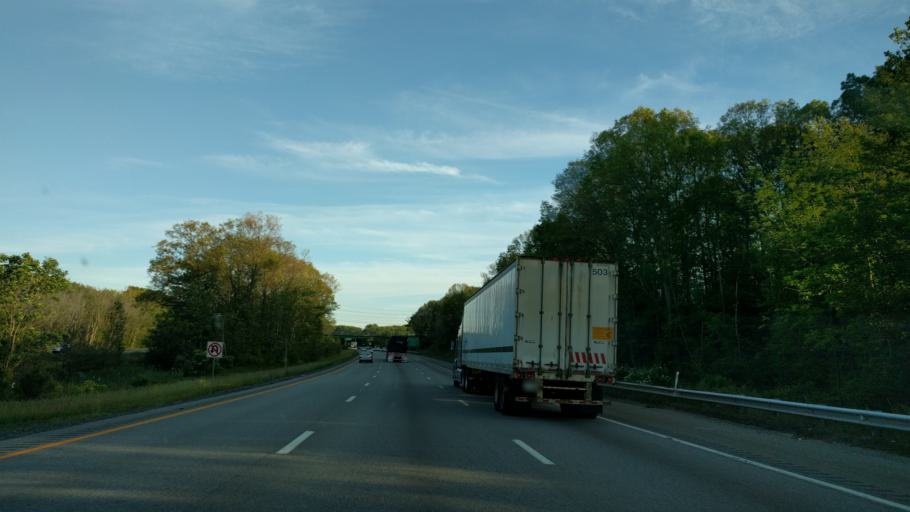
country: US
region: Massachusetts
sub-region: Middlesex County
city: Marlborough
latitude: 42.3357
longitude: -71.5759
